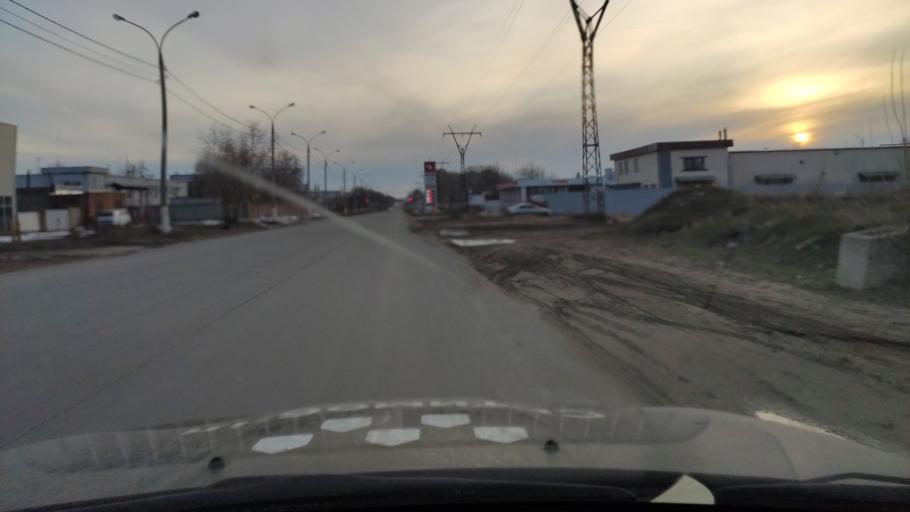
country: RU
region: Samara
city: Zhigulevsk
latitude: 53.4813
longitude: 49.4989
